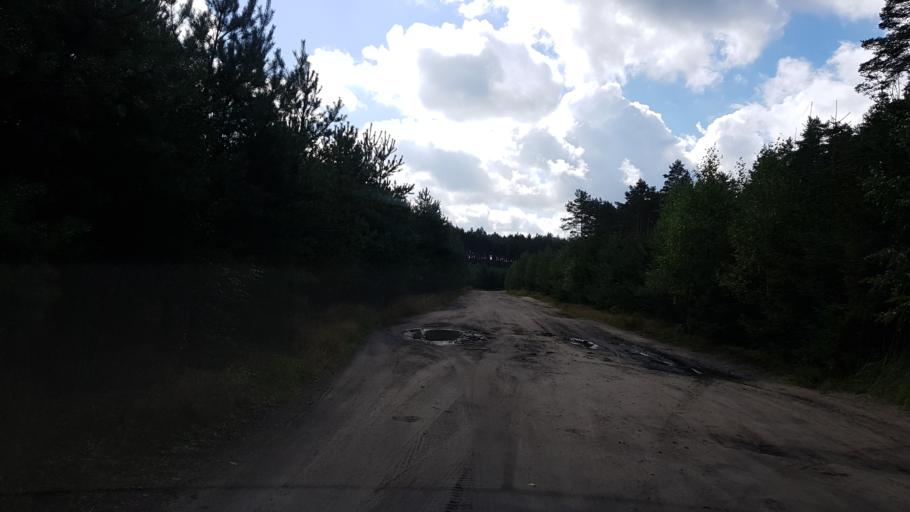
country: PL
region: West Pomeranian Voivodeship
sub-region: Powiat bialogardzki
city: Tychowo
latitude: 54.0441
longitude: 16.3076
